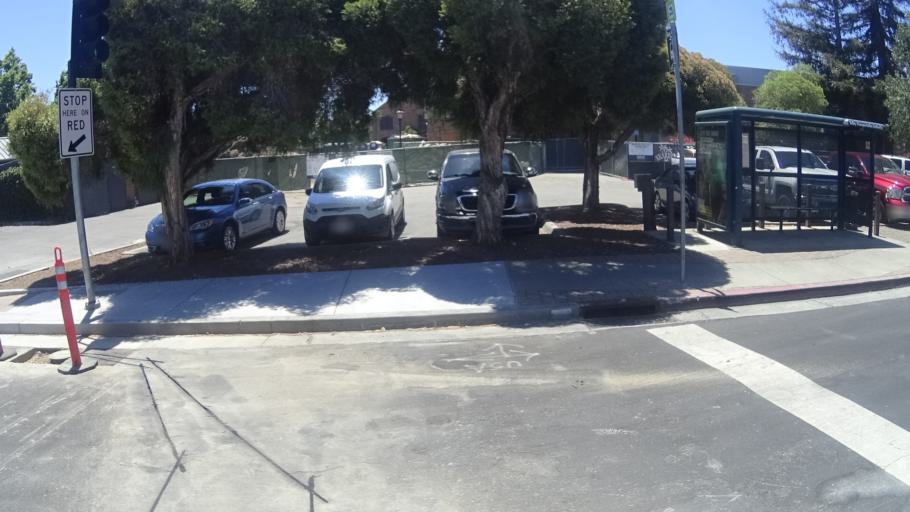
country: US
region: California
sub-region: Santa Clara County
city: Campbell
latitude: 37.2861
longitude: -121.9434
